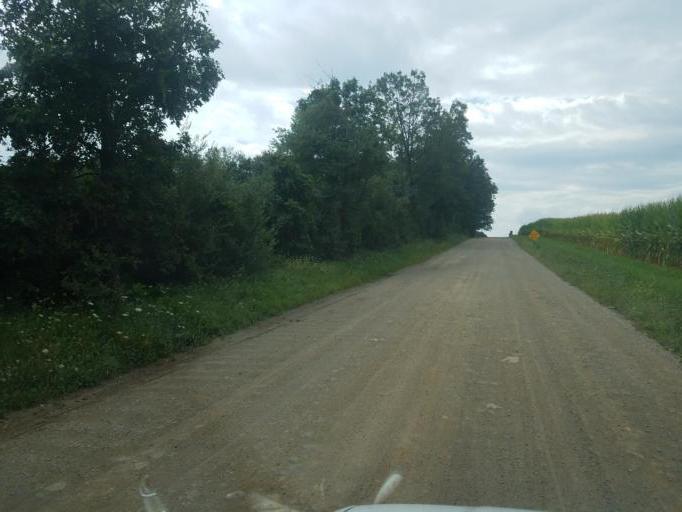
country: US
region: Ohio
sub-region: Knox County
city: Danville
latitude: 40.5502
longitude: -82.3595
